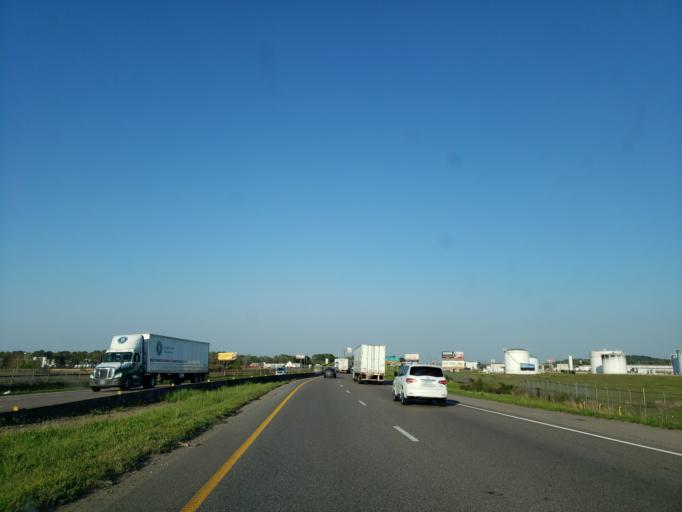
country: US
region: Mississippi
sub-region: Lauderdale County
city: Meridian
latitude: 32.3484
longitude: -88.7501
